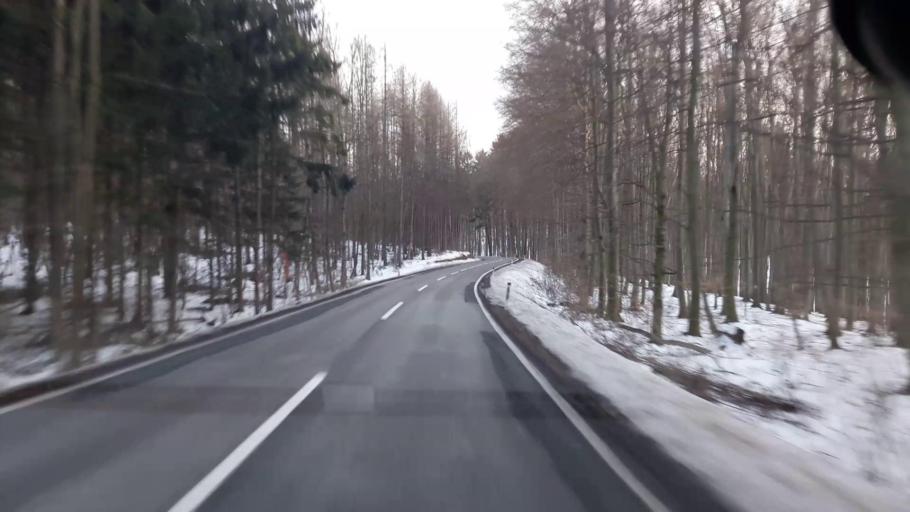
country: AT
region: Lower Austria
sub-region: Politischer Bezirk Wien-Umgebung
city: Mauerbach
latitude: 48.2755
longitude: 16.1850
